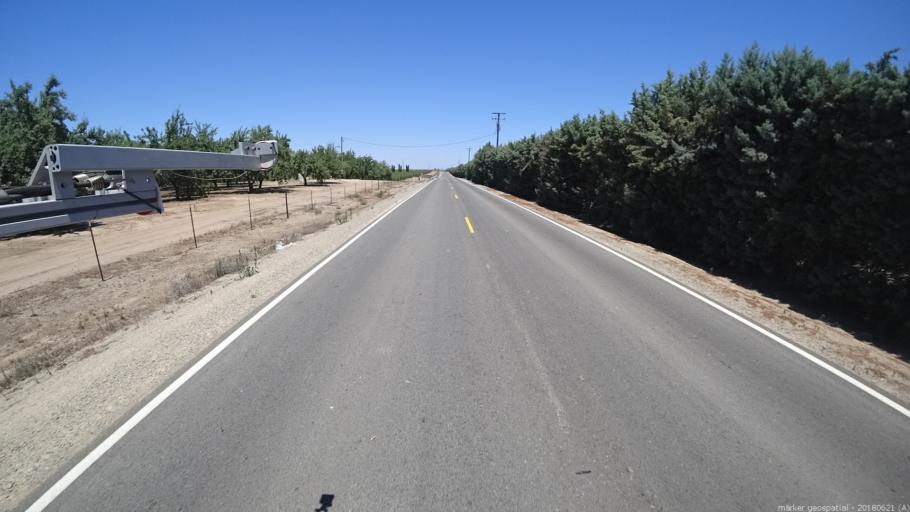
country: US
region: California
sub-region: Madera County
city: Bonadelle Ranchos-Madera Ranchos
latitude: 36.8905
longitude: -119.8934
